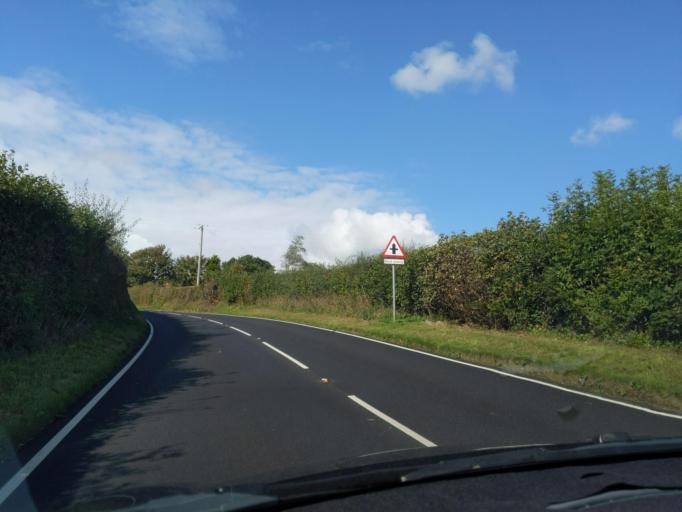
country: GB
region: England
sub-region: Devon
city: Holsworthy
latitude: 50.8017
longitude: -4.3425
